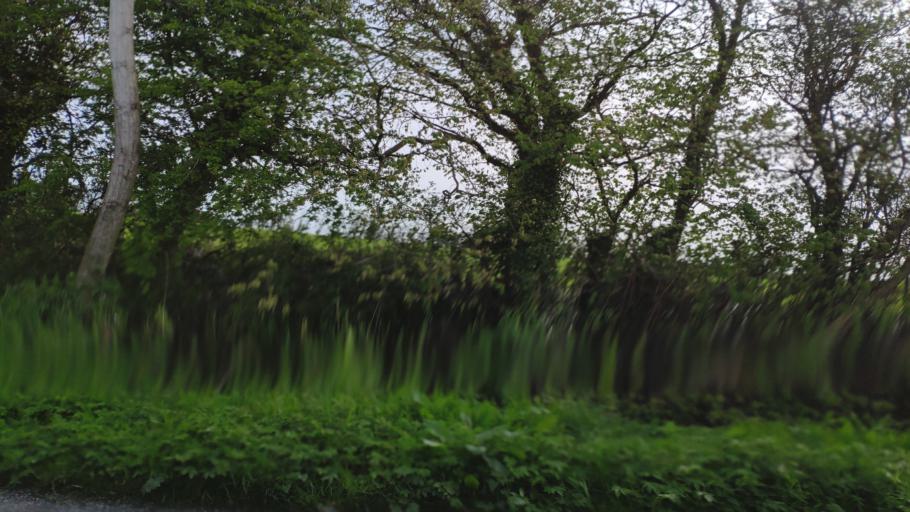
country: IE
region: Munster
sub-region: County Cork
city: Blarney
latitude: 51.9643
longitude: -8.5144
